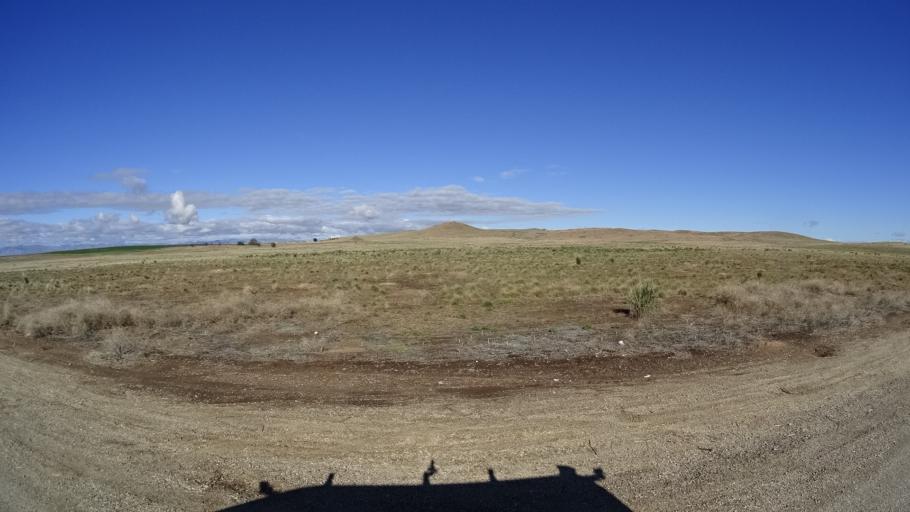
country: US
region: Idaho
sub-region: Ada County
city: Kuna
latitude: 43.4336
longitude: -116.4140
